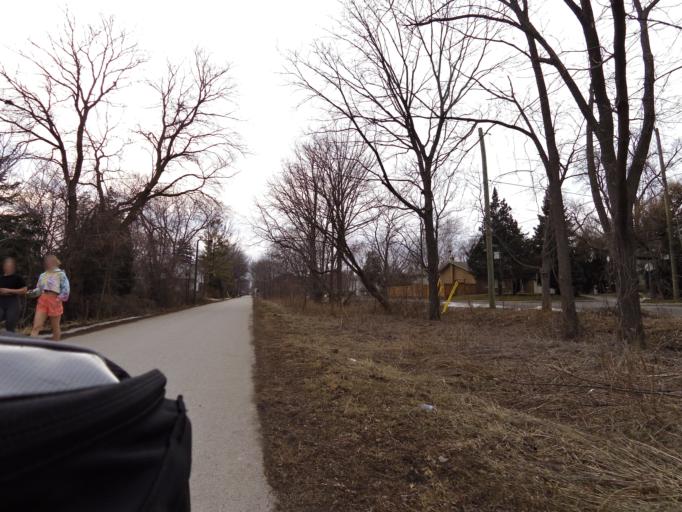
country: CA
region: Ontario
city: Hamilton
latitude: 43.2539
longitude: -79.9173
